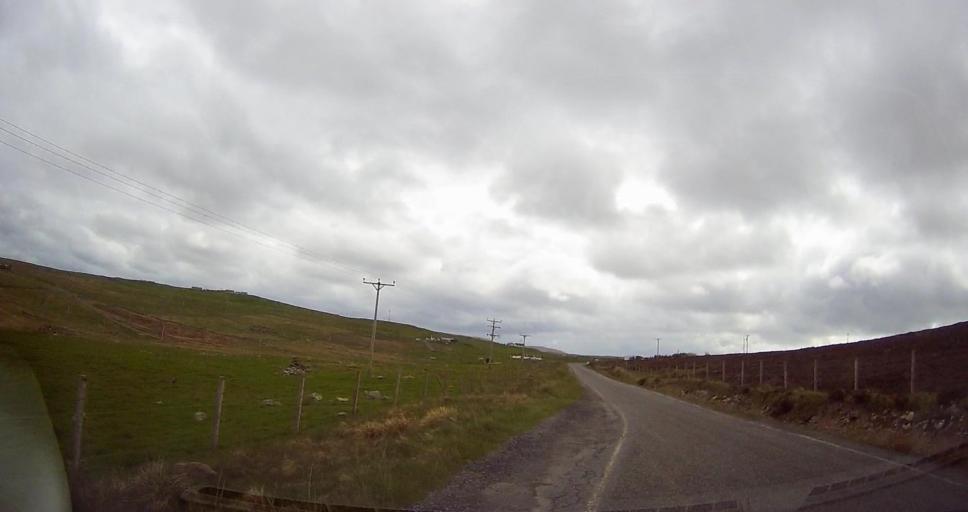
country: GB
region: Scotland
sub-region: Shetland Islands
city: Sandwick
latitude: 60.2460
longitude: -1.5108
